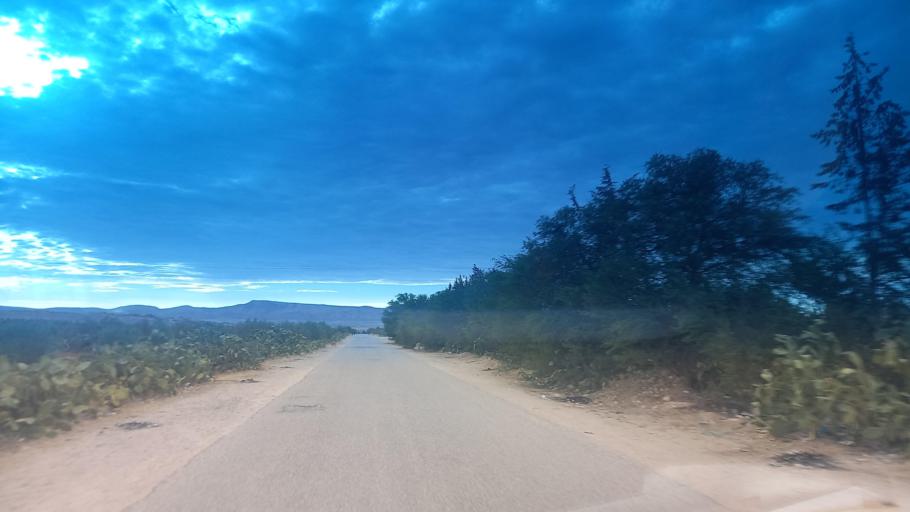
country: TN
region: Al Qasrayn
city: Sbiba
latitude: 35.3805
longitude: 9.0551
